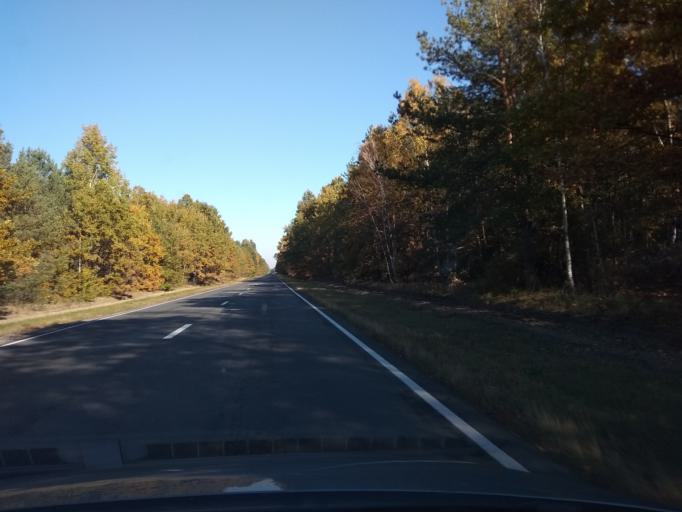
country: BY
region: Brest
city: Kobryn
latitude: 52.0400
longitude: 24.2730
